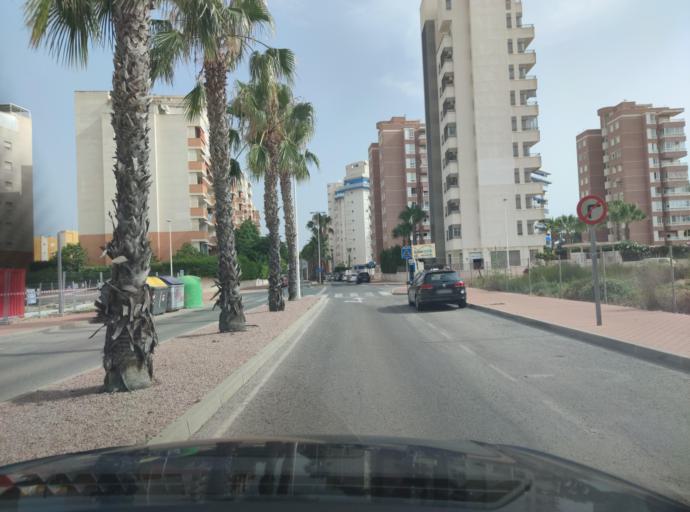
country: ES
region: Valencia
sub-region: Provincia de Alicante
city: Guardamar del Segura
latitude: 38.0997
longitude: -0.6556
